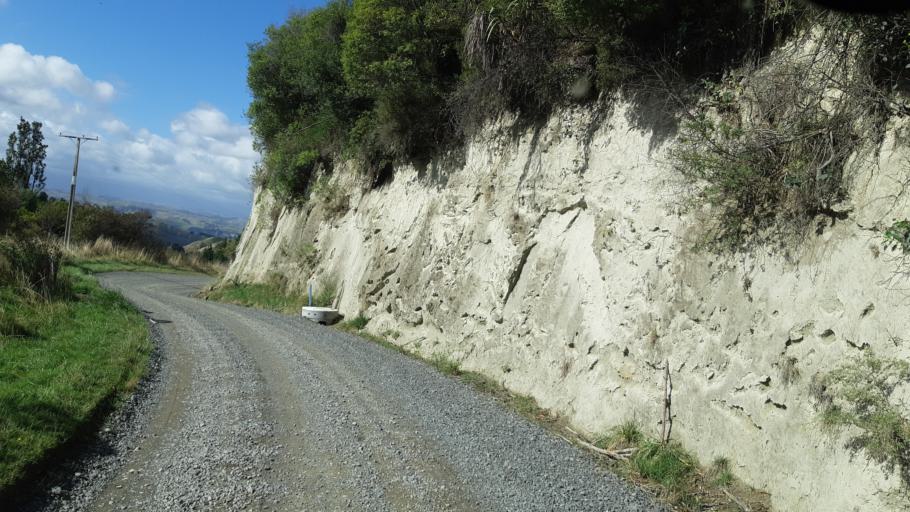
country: NZ
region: Manawatu-Wanganui
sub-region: Ruapehu District
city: Waiouru
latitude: -39.8423
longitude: 175.6579
